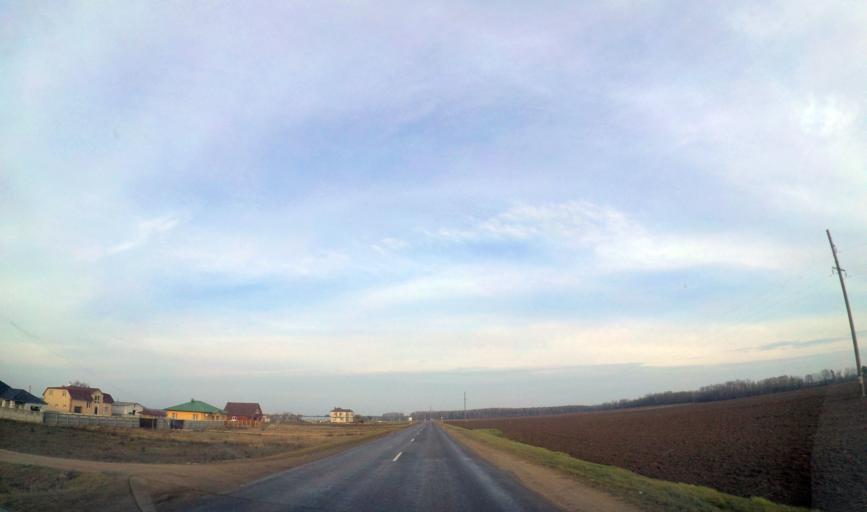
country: BY
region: Grodnenskaya
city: Hrodna
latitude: 53.7445
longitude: 23.9351
